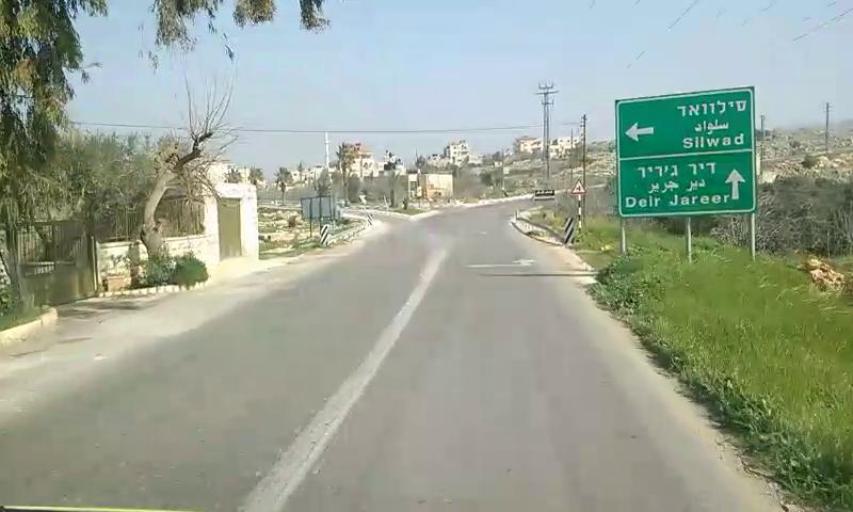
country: PS
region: West Bank
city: Silwad
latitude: 31.9629
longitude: 35.2631
